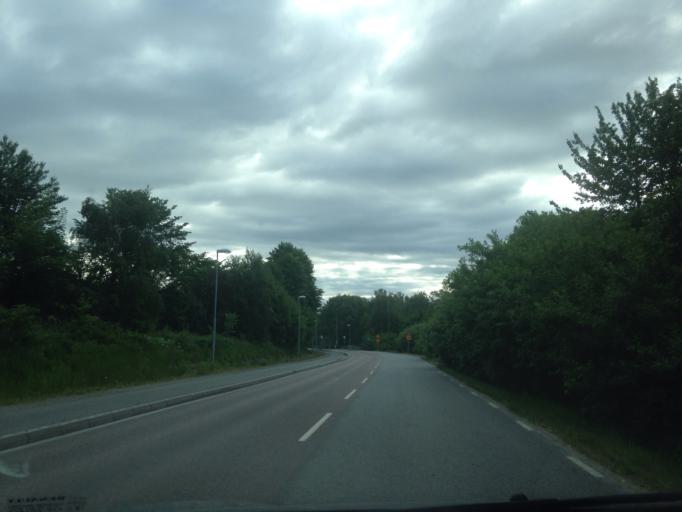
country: SE
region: Vaestra Goetaland
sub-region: Goteborg
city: Torslanda
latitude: 57.7633
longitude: 11.8182
